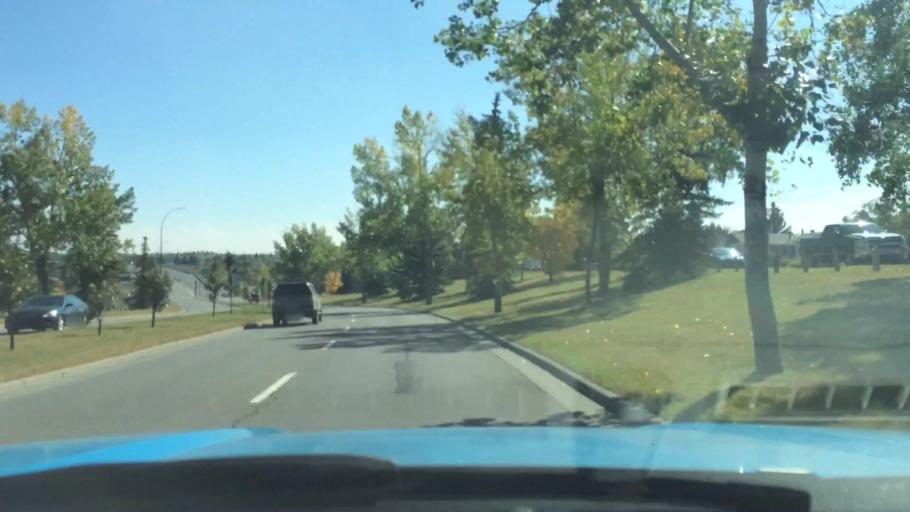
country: CA
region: Alberta
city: Calgary
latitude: 50.9134
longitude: -114.0781
